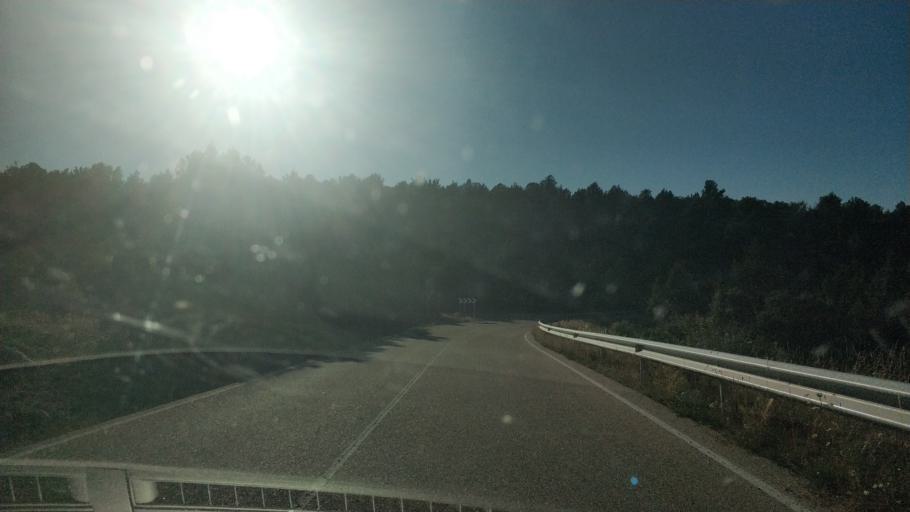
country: ES
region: Castille and Leon
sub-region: Provincia de Soria
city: Montejo de Tiermes
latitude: 41.4268
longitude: -3.2032
